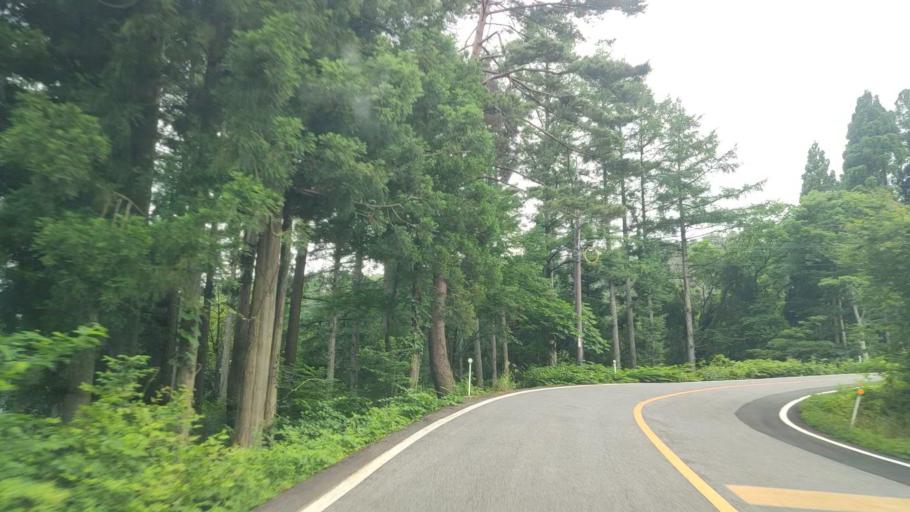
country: JP
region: Tottori
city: Yonago
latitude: 35.3321
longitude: 133.5571
